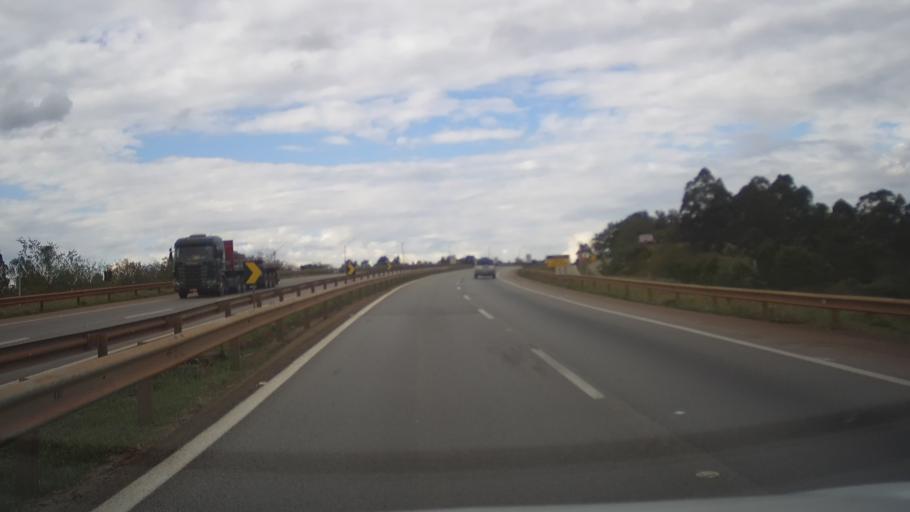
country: BR
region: Minas Gerais
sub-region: Itauna
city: Itauna
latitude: -20.3051
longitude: -44.4468
